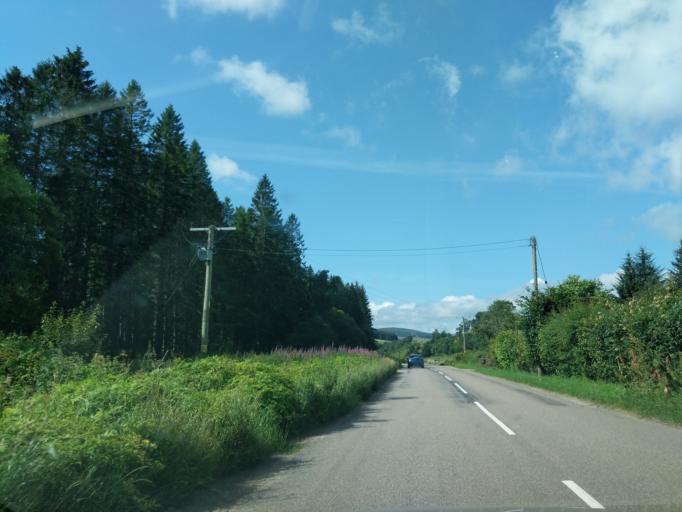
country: GB
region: Scotland
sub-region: Moray
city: Dufftown
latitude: 57.3572
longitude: -3.2918
